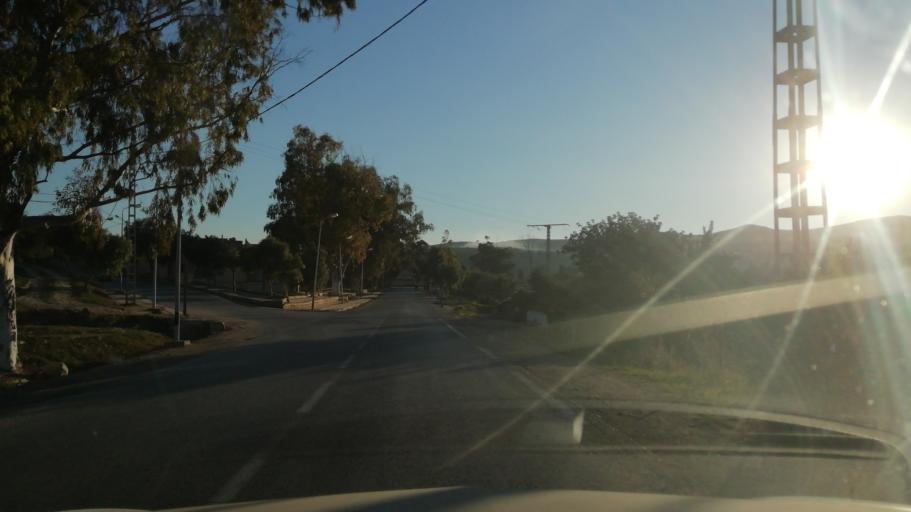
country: DZ
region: Tlemcen
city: Nedroma
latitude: 34.8272
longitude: -1.6501
